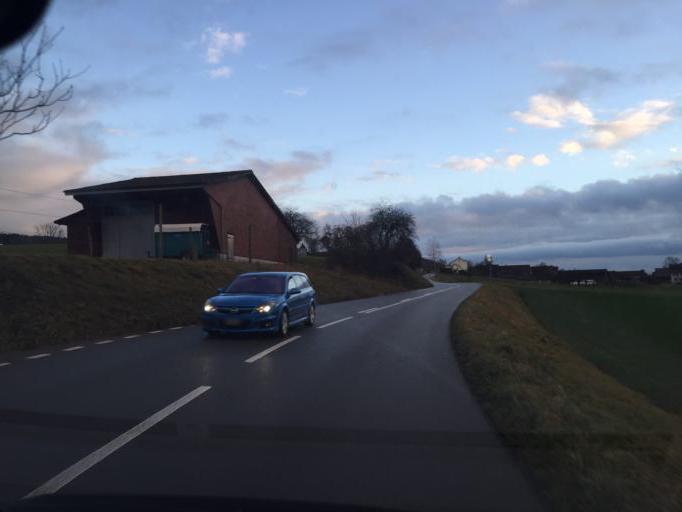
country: DE
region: Baden-Wuerttemberg
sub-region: Freiburg Region
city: Busingen
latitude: 47.7106
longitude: 8.7162
